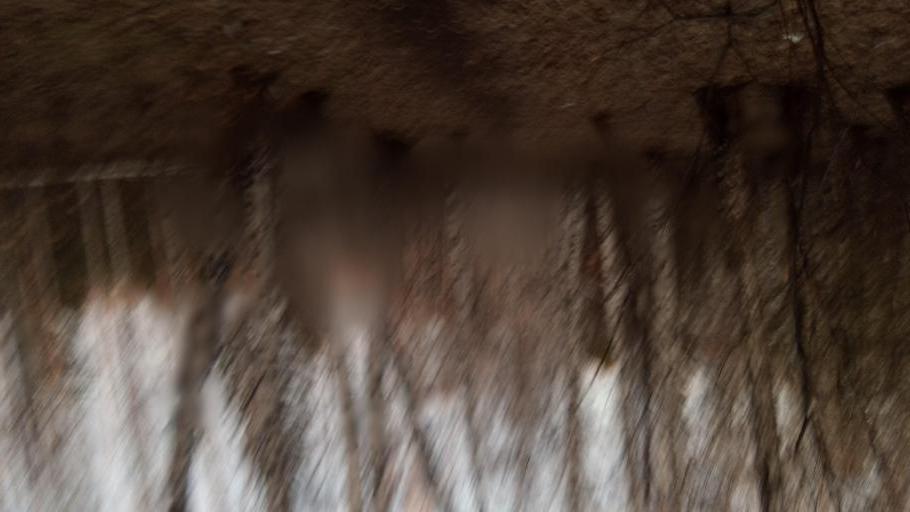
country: RU
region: Chelyabinsk
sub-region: Gorod Chelyabinsk
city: Chelyabinsk
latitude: 55.1578
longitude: 61.3275
